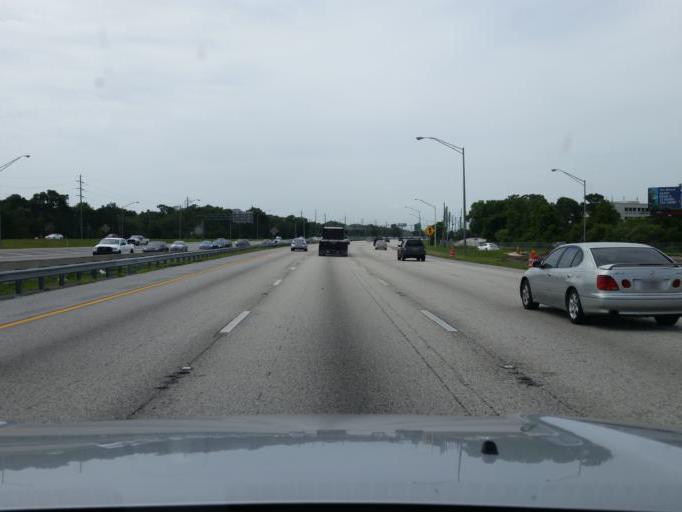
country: US
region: Florida
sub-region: Orange County
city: Eatonville
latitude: 28.6297
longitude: -81.3874
